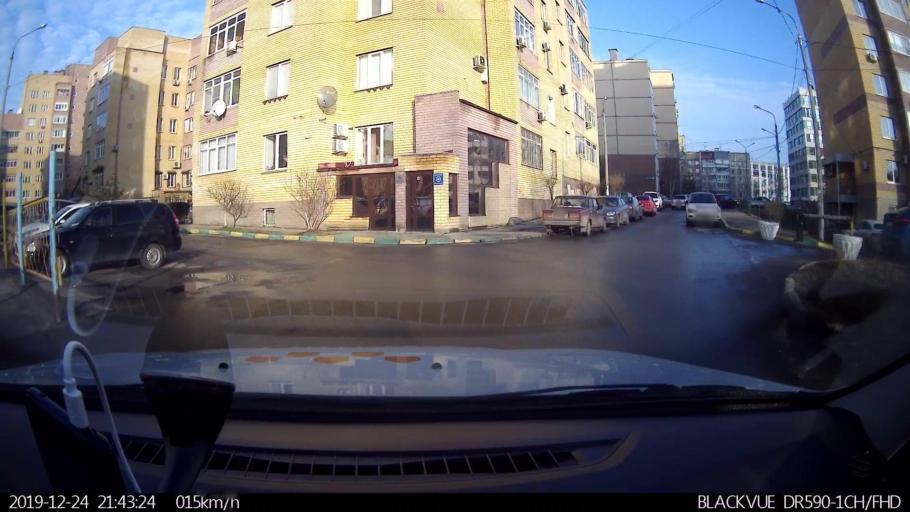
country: RU
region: Nizjnij Novgorod
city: Nizhniy Novgorod
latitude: 56.3332
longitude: 43.9568
